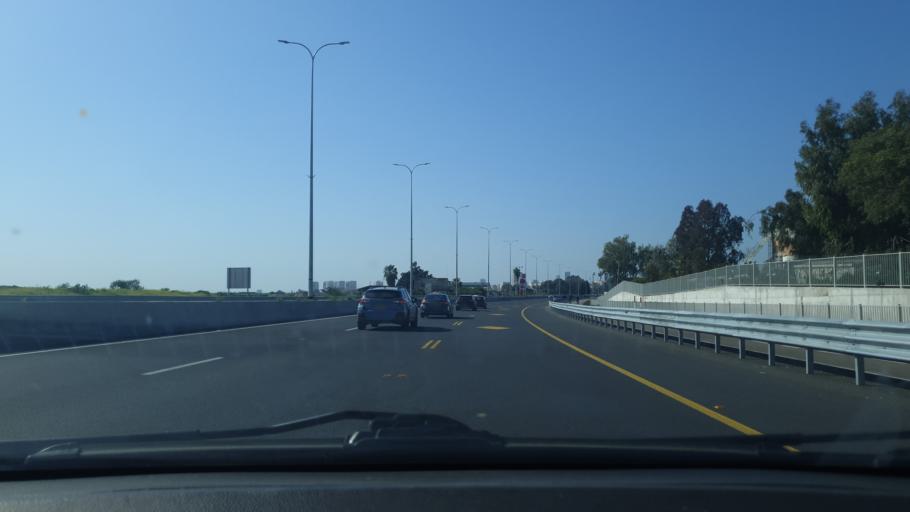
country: IL
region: Tel Aviv
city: Azor
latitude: 32.0389
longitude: 34.8262
